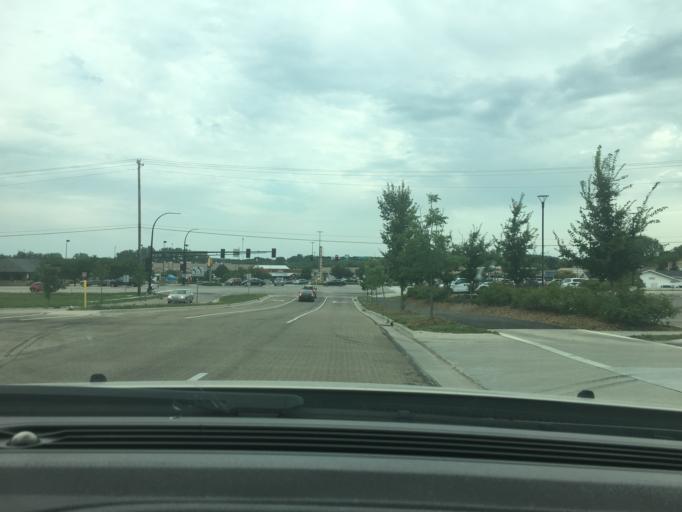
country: US
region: Minnesota
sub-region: Olmsted County
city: Rochester
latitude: 44.0805
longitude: -92.5148
